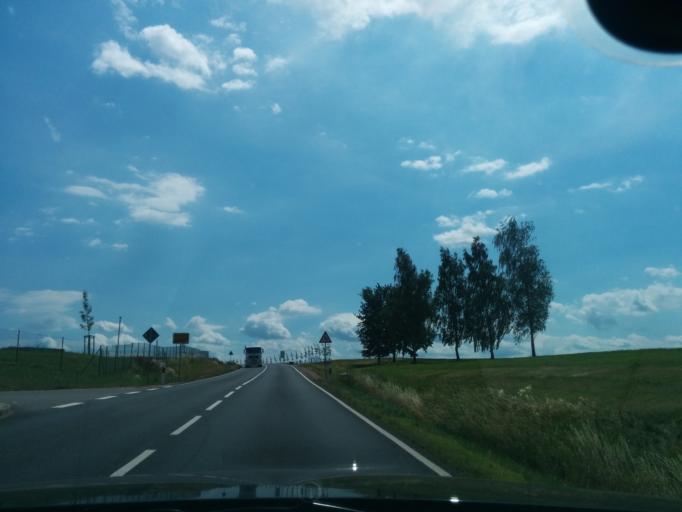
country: DE
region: Saxony
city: Hainichen
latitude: 51.0243
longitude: 13.1165
